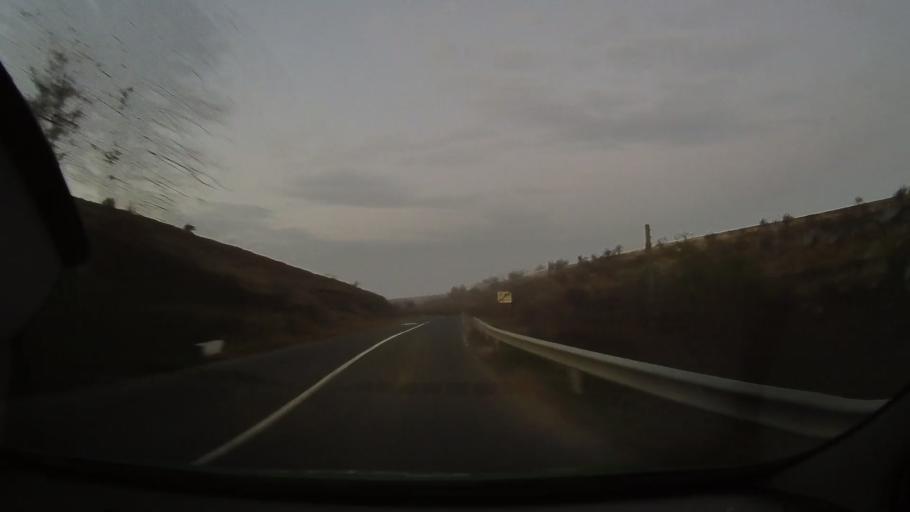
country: RO
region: Constanta
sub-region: Comuna Ion Corvin
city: Ion Corvin
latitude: 44.1001
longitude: 27.7548
